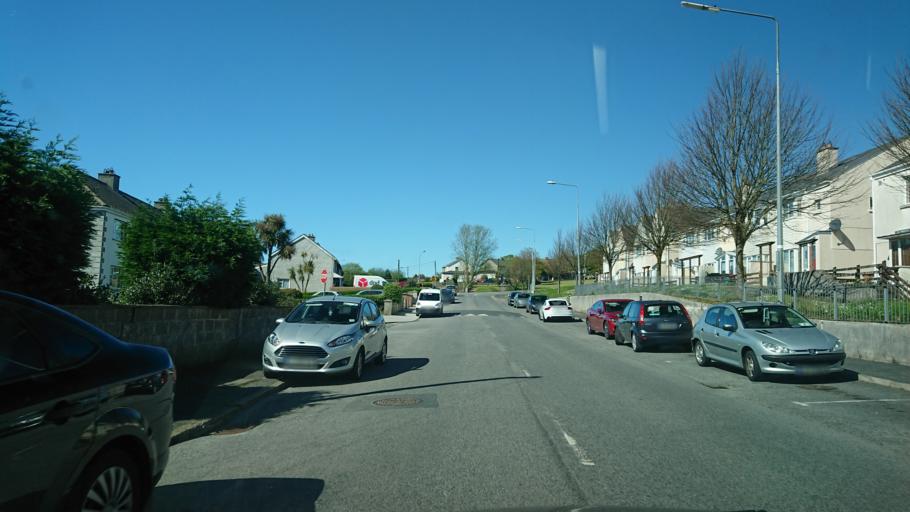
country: IE
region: Munster
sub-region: Waterford
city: Waterford
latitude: 52.2508
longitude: -7.1254
